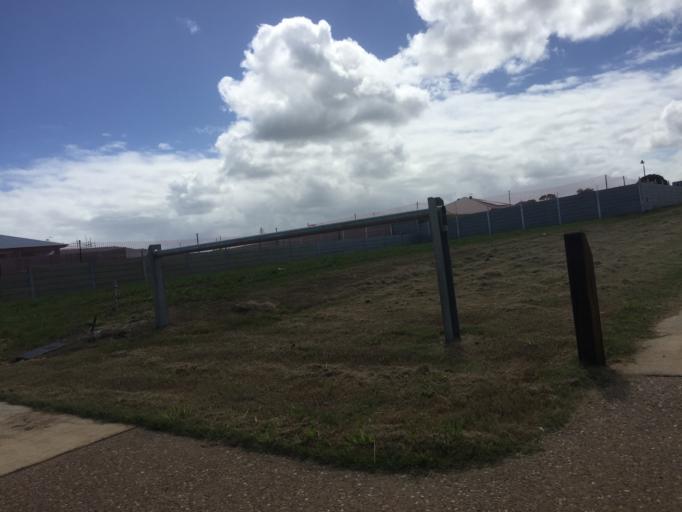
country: AU
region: Queensland
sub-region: Moreton Bay
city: Morayfield
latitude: -27.1115
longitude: 152.9294
